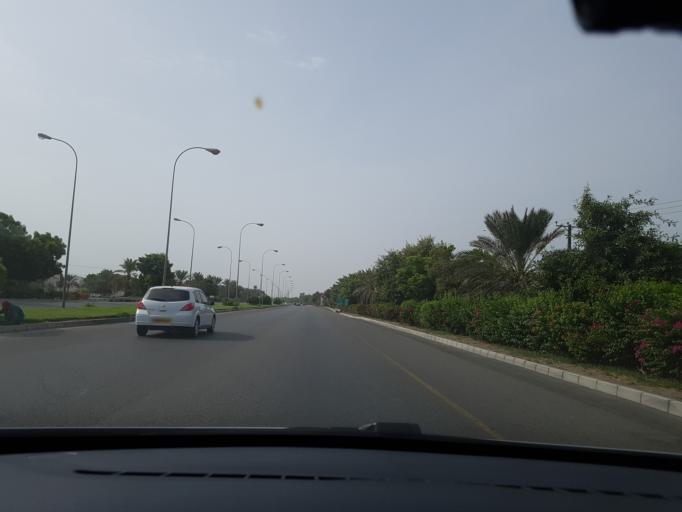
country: OM
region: Al Batinah
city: Al Sohar
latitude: 24.3750
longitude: 56.7035
